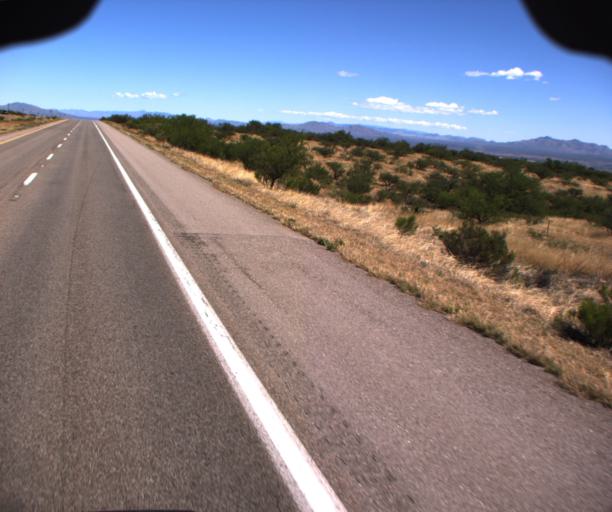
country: US
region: Arizona
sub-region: Cochise County
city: Whetstone
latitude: 31.8880
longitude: -110.3410
